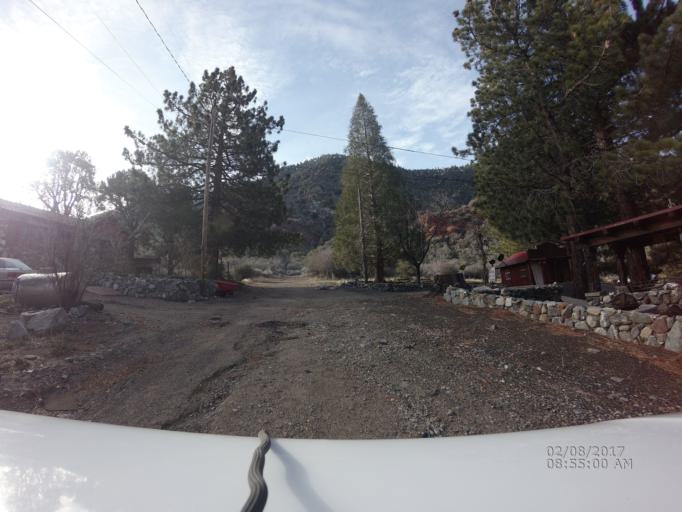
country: US
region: California
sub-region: San Bernardino County
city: Pinon Hills
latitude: 34.3946
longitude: -117.8072
